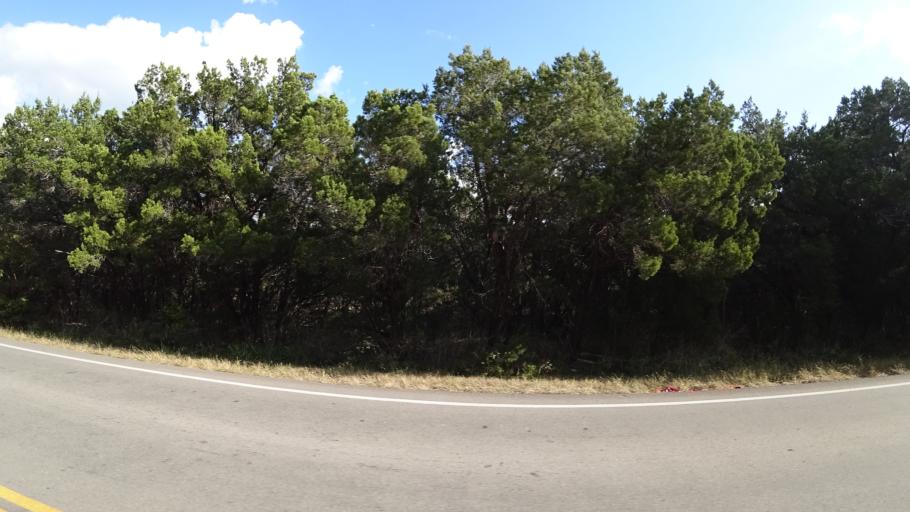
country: US
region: Texas
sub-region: Travis County
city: Barton Creek
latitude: 30.2691
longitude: -97.8876
